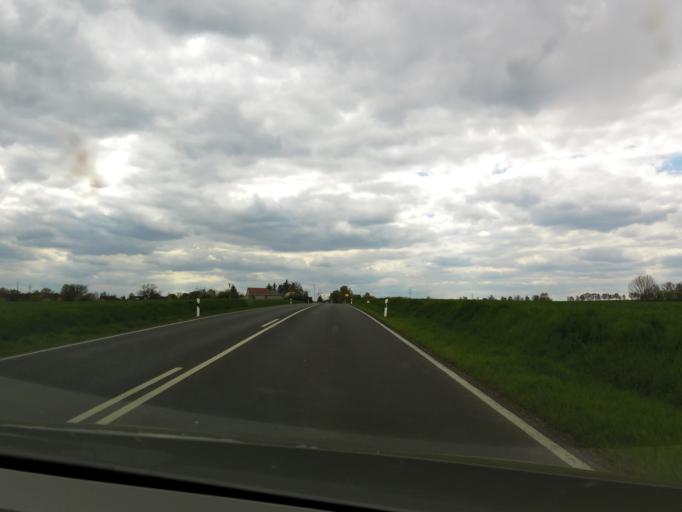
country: DE
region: Thuringia
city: Rannstedt
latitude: 51.0909
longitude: 11.5411
